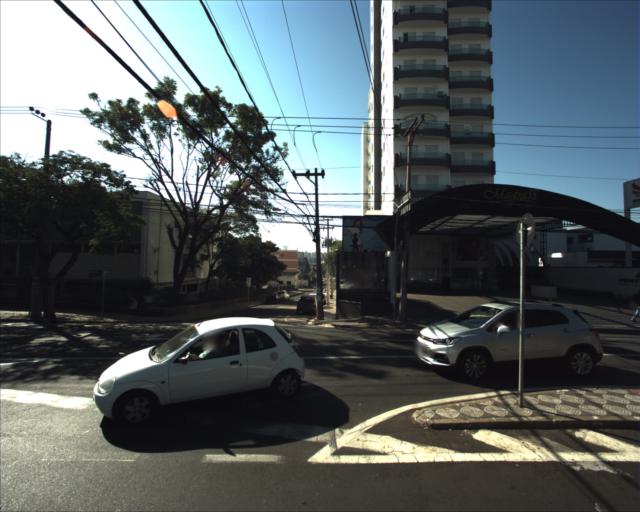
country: BR
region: Sao Paulo
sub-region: Sorocaba
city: Sorocaba
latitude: -23.5072
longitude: -47.4558
